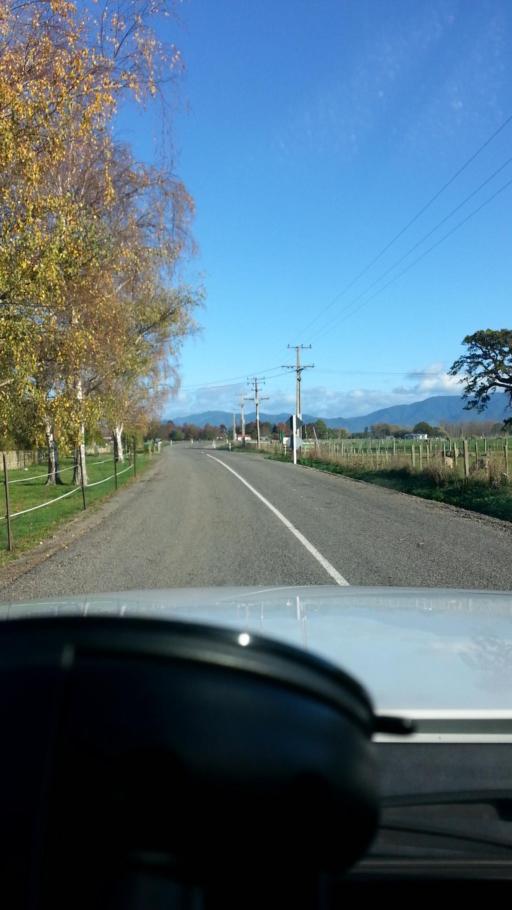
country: NZ
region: Wellington
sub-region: Masterton District
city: Masterton
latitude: -41.0956
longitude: 175.4844
